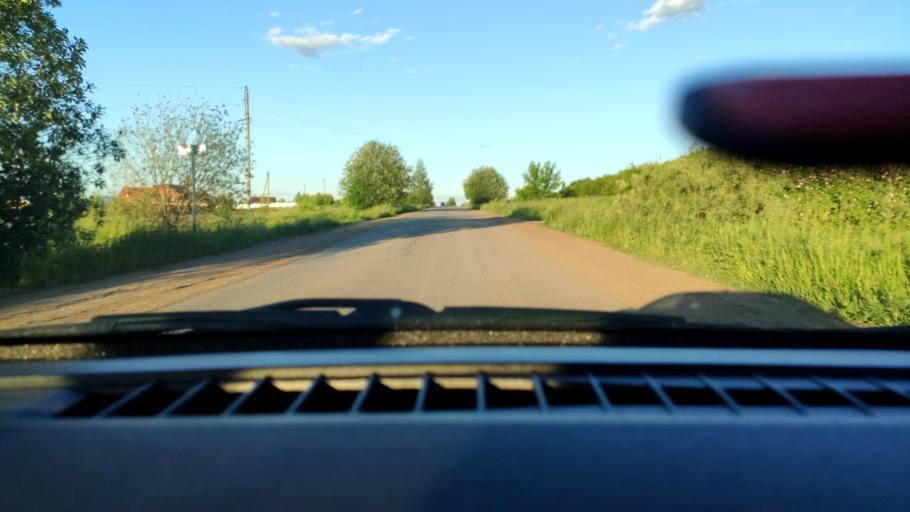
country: RU
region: Perm
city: Kultayevo
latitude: 57.9291
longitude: 55.8641
